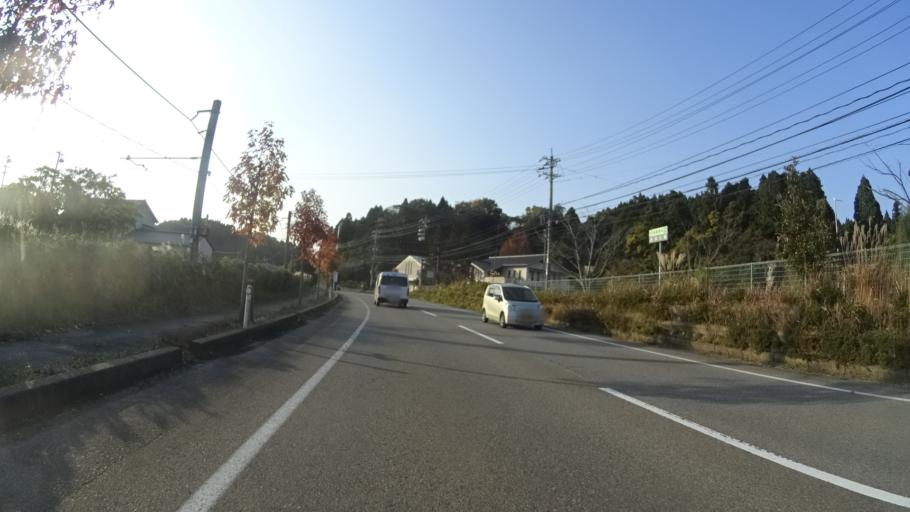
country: JP
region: Ishikawa
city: Nanao
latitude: 37.0572
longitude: 136.9515
